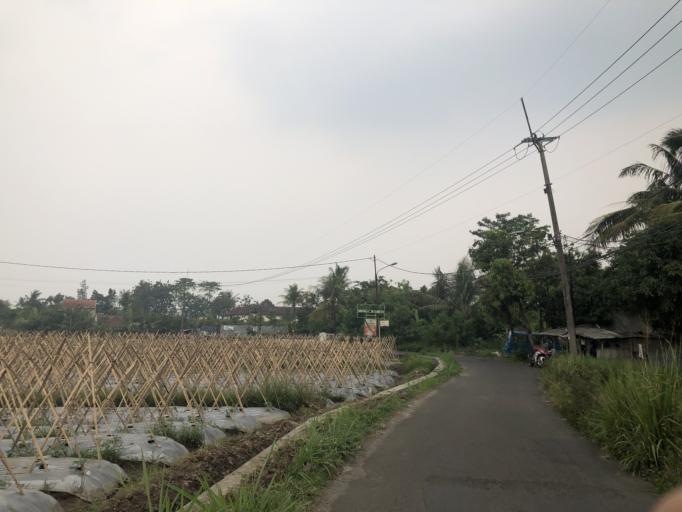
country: ID
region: West Java
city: Ciampea
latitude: -6.5669
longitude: 106.7459
